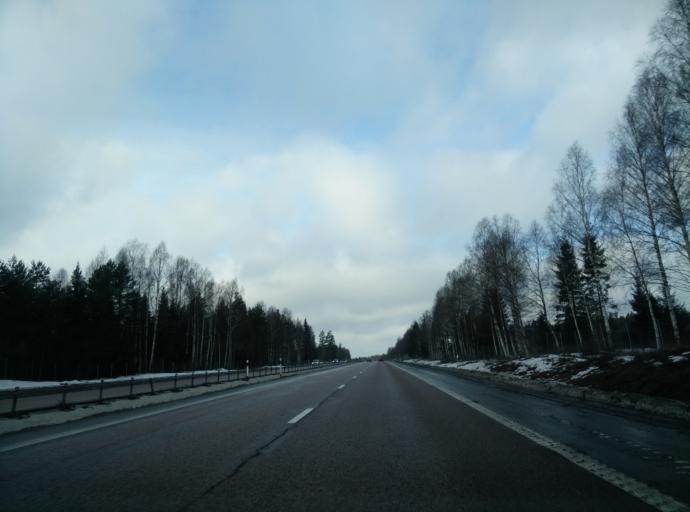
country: SE
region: Gaevleborg
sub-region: Gavle Kommun
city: Valbo
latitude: 60.6280
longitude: 16.9388
